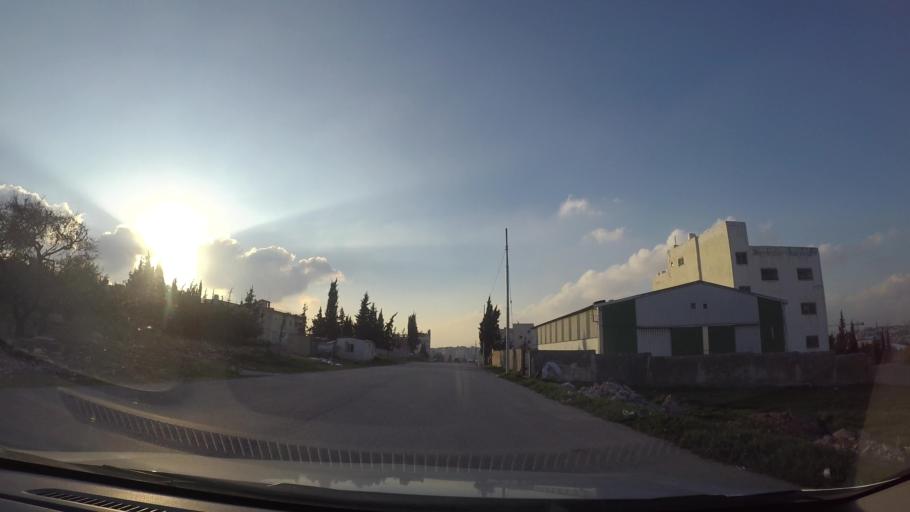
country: JO
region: Amman
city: Al Bunayyat ash Shamaliyah
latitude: 31.9104
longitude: 35.9167
